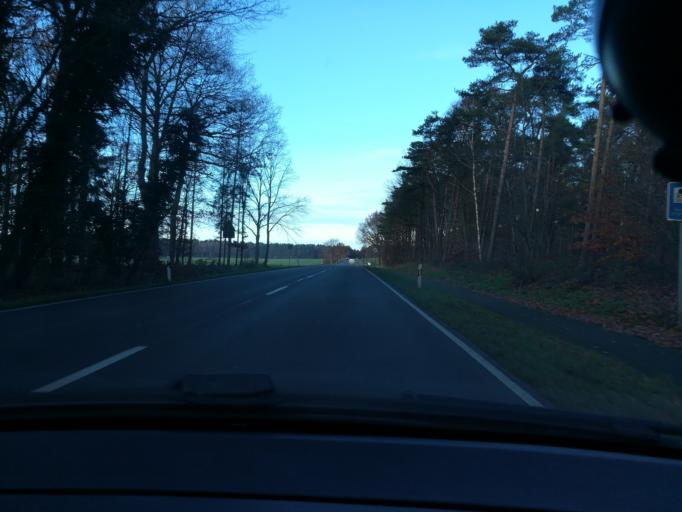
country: DE
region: Lower Saxony
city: Kirchdorf
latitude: 52.5715
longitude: 8.8470
